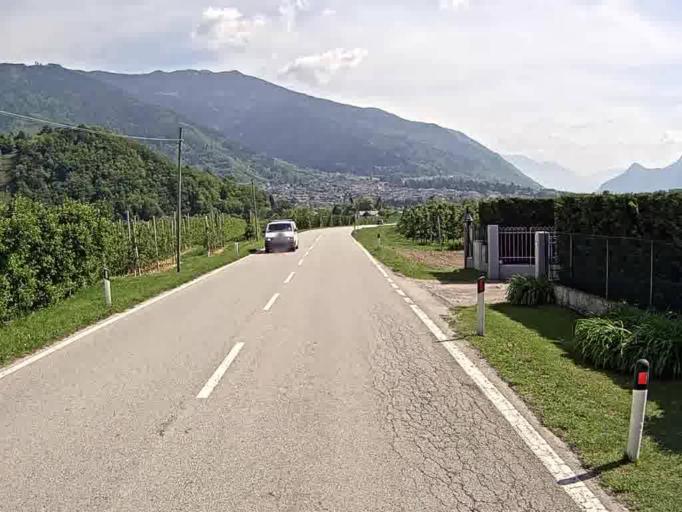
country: IT
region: Trentino-Alto Adige
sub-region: Provincia di Trento
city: Caldonazzo
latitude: 45.9983
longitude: 11.2798
